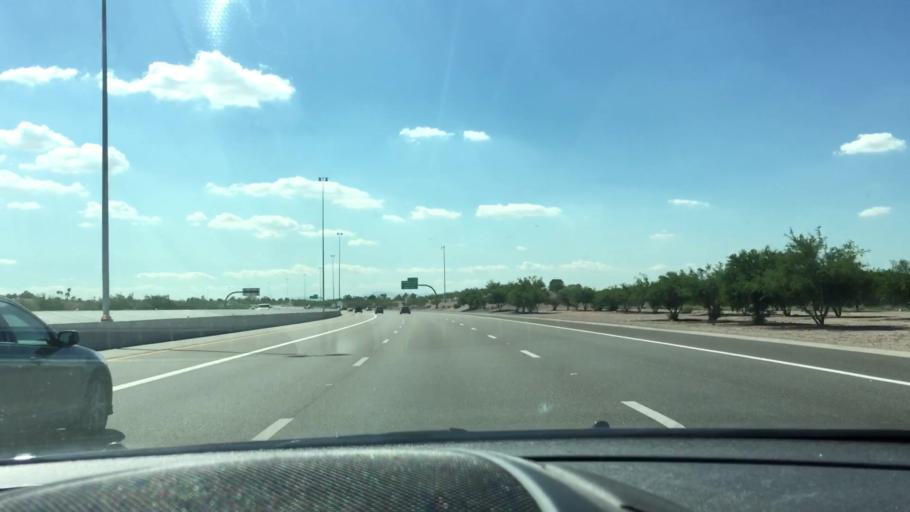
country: US
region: Arizona
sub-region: Maricopa County
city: Mesa
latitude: 33.4791
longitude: -111.7733
